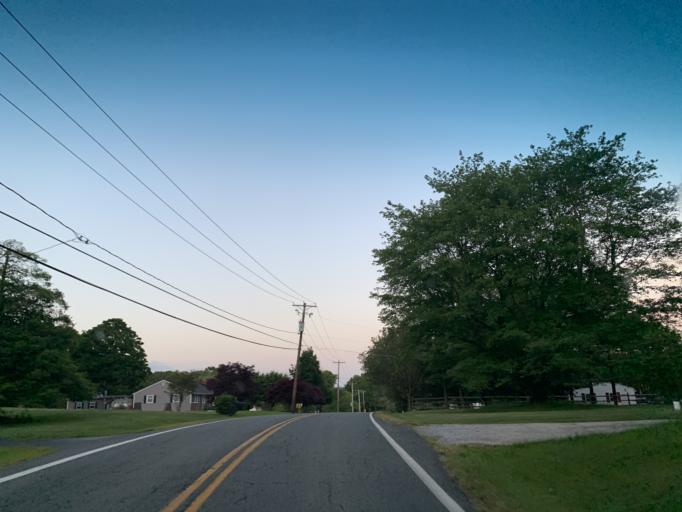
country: US
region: Maryland
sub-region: Cecil County
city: Perryville
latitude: 39.6194
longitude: -76.0583
